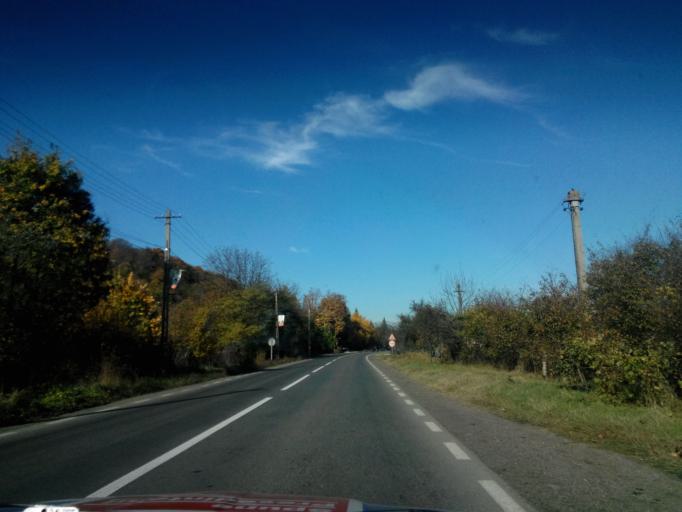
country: RO
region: Bacau
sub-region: Comuna Stefan Cel Mare
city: Stefan Cel Mare
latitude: 46.1992
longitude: 26.8889
